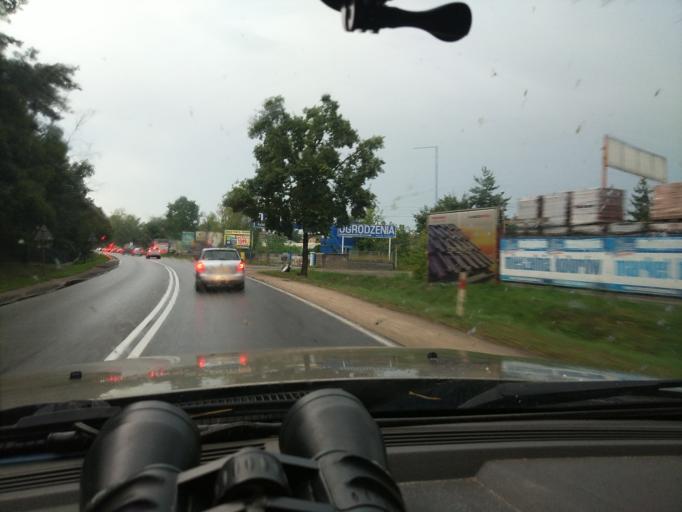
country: PL
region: Masovian Voivodeship
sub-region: Powiat pruszkowski
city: Granica
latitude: 52.1477
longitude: 20.7897
